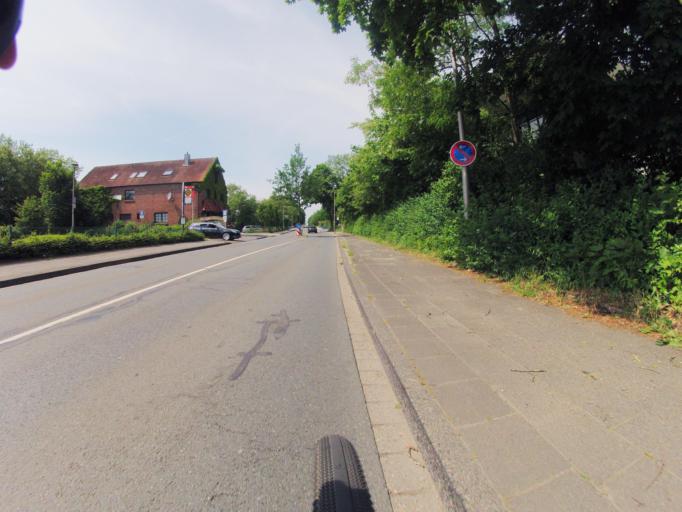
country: DE
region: North Rhine-Westphalia
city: Ibbenburen
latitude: 52.2776
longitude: 7.7214
